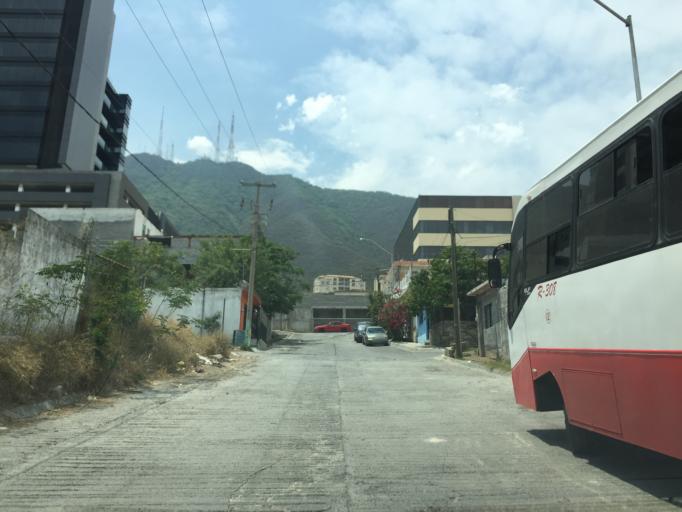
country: MX
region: Nuevo Leon
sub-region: Monterrey
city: Monterrey
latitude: 25.6357
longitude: -100.3125
